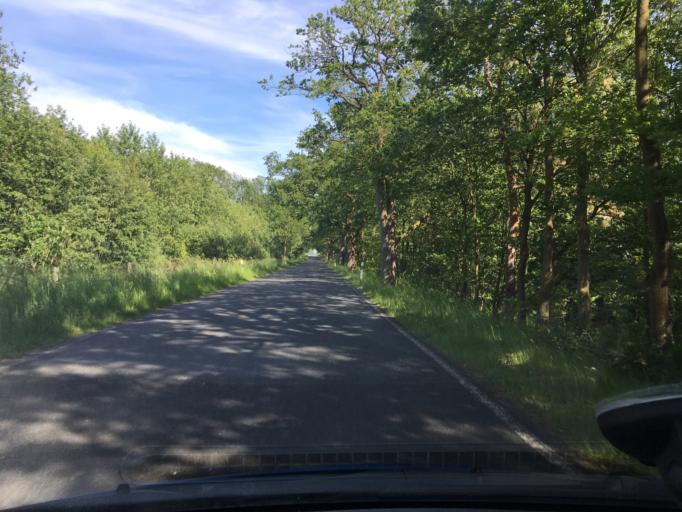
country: DE
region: Lower Saxony
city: Neu Darchau
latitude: 53.3318
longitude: 10.8740
